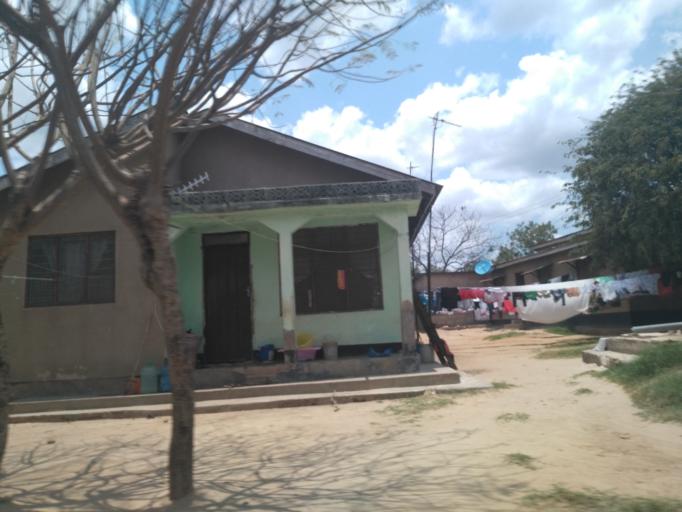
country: TZ
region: Dar es Salaam
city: Dar es Salaam
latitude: -6.8370
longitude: 39.3229
